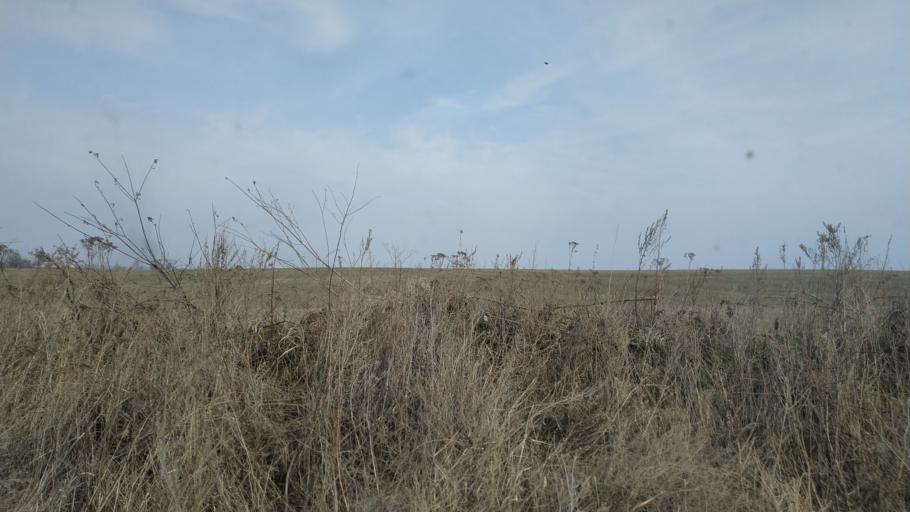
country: RU
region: Moskovskaya
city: Troitskoye
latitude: 55.3575
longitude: 38.4654
